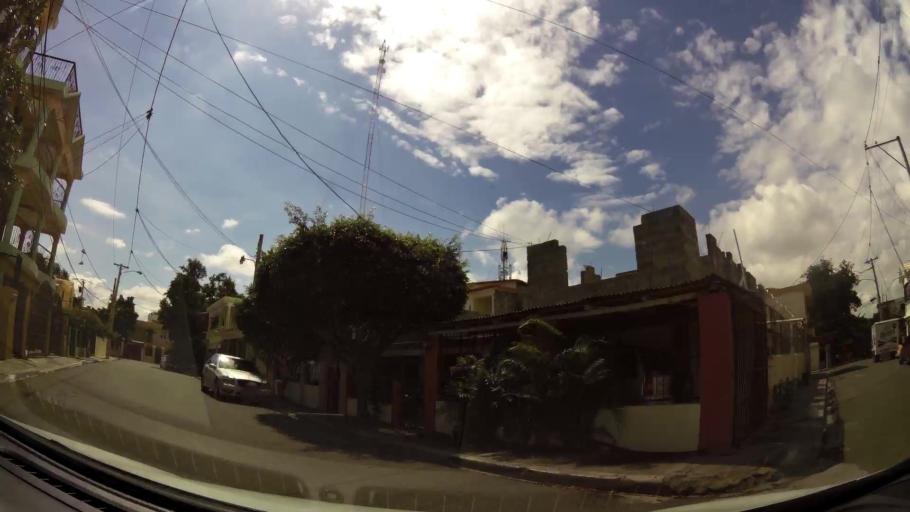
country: DO
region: Santiago
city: Santiago de los Caballeros
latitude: 19.4705
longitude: -70.6986
